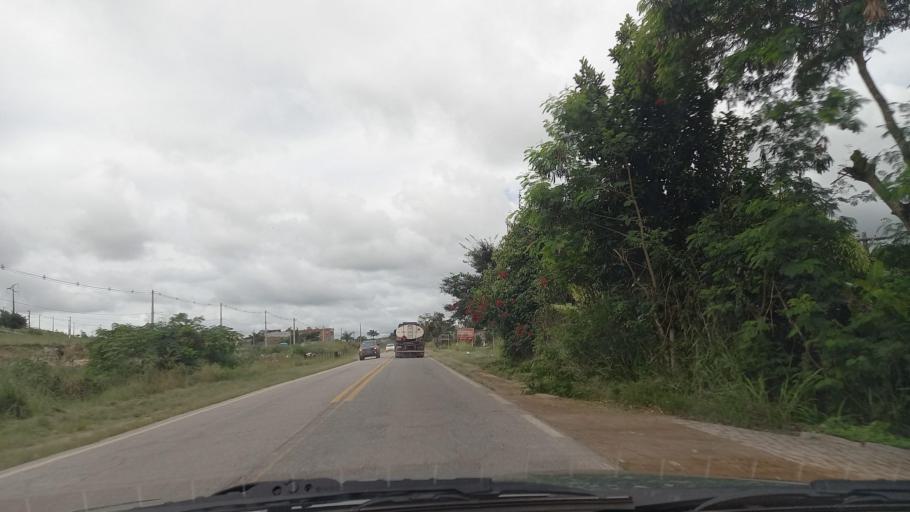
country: BR
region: Pernambuco
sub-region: Canhotinho
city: Canhotinho
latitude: -8.8745
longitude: -36.2042
